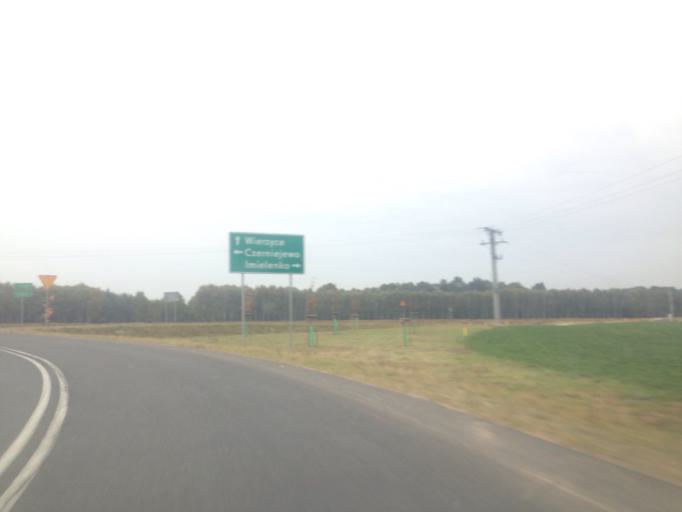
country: PL
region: Greater Poland Voivodeship
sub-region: Powiat gnieznienski
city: Lubowo
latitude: 52.4744
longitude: 17.4076
